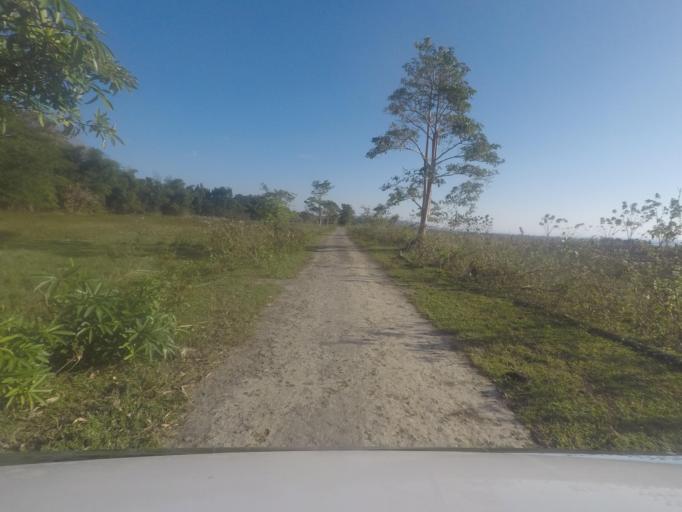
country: TL
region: Lautem
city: Lospalos
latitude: -8.4364
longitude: 127.1848
